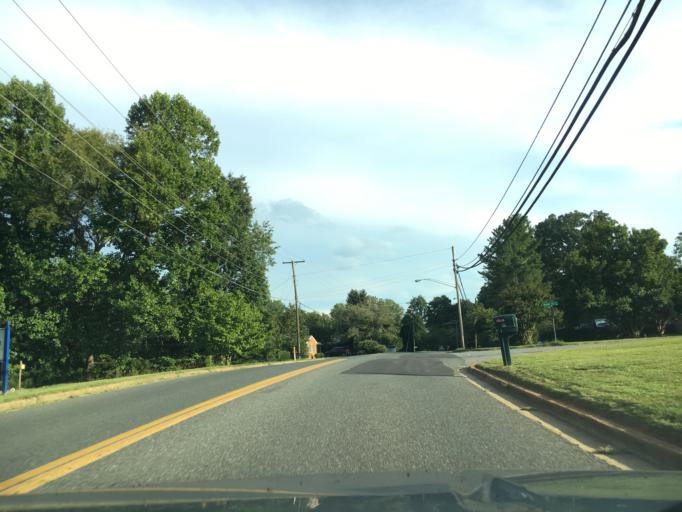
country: US
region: Virginia
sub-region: City of Lynchburg
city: West Lynchburg
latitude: 37.4193
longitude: -79.2089
